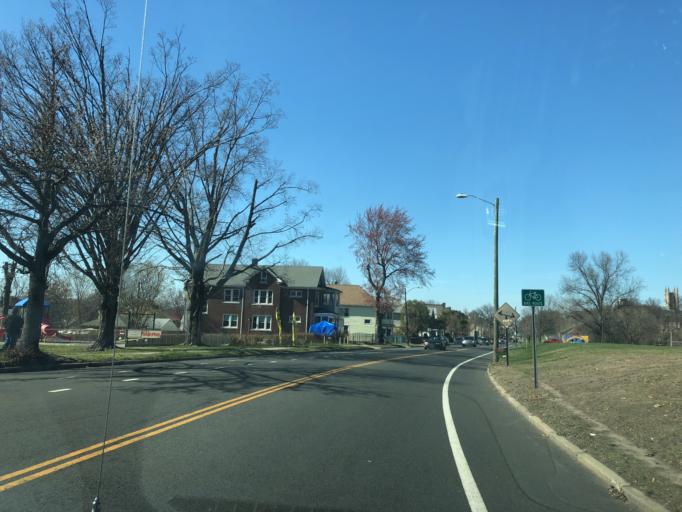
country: US
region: Connecticut
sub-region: Hartford County
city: Hartford
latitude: 41.7427
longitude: -72.6940
